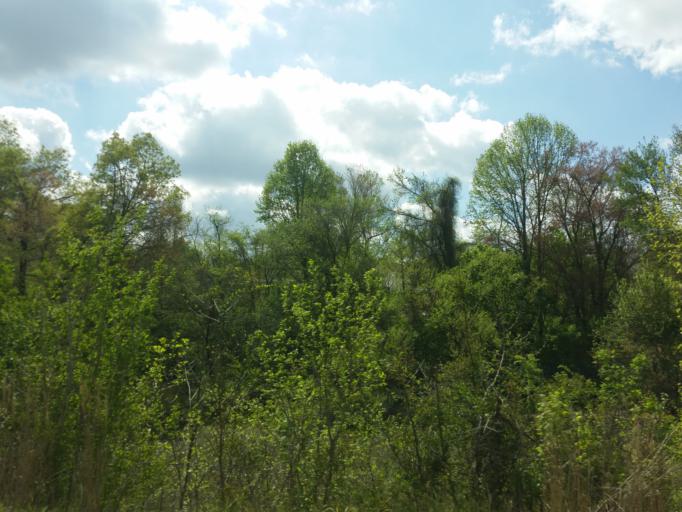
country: US
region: Kentucky
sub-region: Bell County
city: Middlesboro
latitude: 36.6206
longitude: -83.7361
